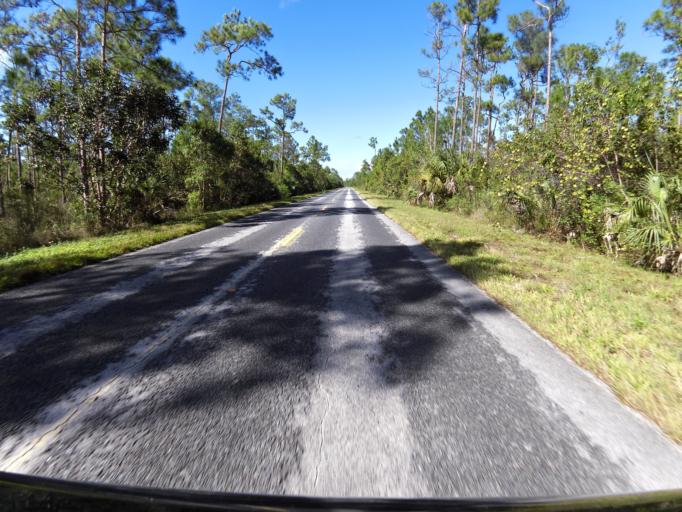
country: US
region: Florida
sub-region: Miami-Dade County
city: Florida City
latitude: 25.4284
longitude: -80.6868
